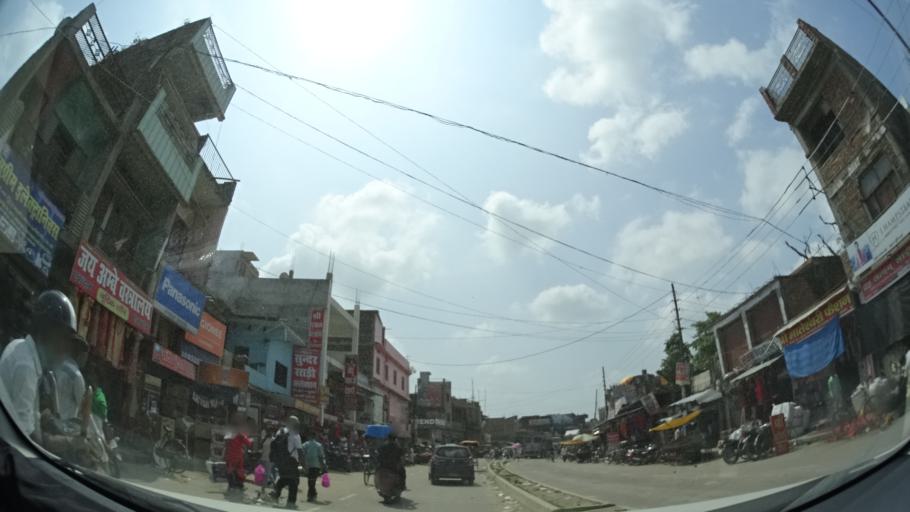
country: NP
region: Western Region
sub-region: Lumbini Zone
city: Bhairahawa
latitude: 27.4743
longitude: 83.4695
